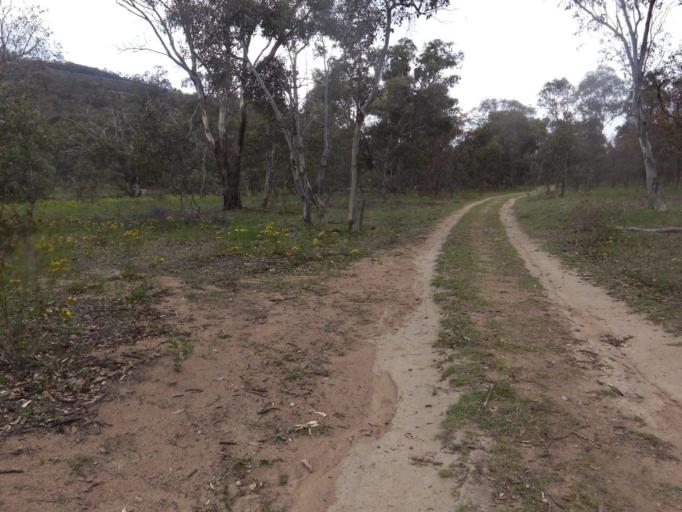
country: AU
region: Australian Capital Territory
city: Forrest
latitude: -35.3540
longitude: 149.1201
